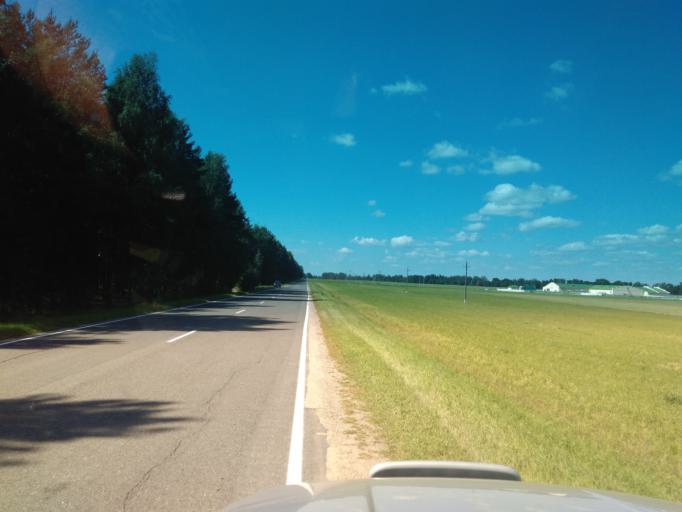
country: BY
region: Minsk
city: Stan'kava
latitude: 53.6242
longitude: 27.2831
